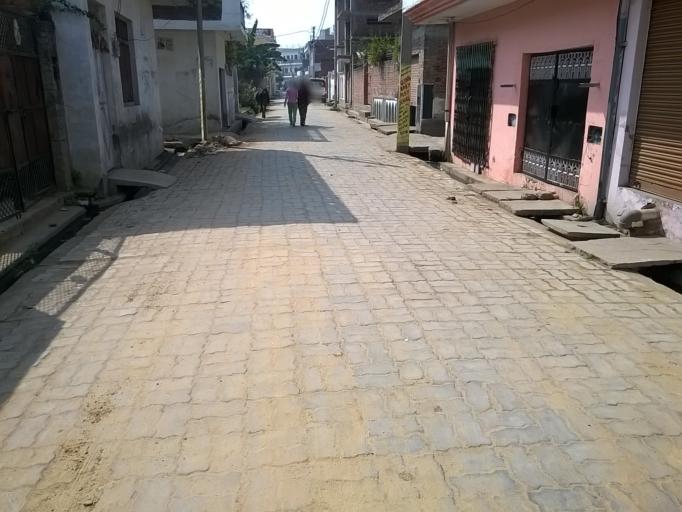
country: IN
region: Uttar Pradesh
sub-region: Etawah
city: Etawah
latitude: 26.7911
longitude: 79.0408
